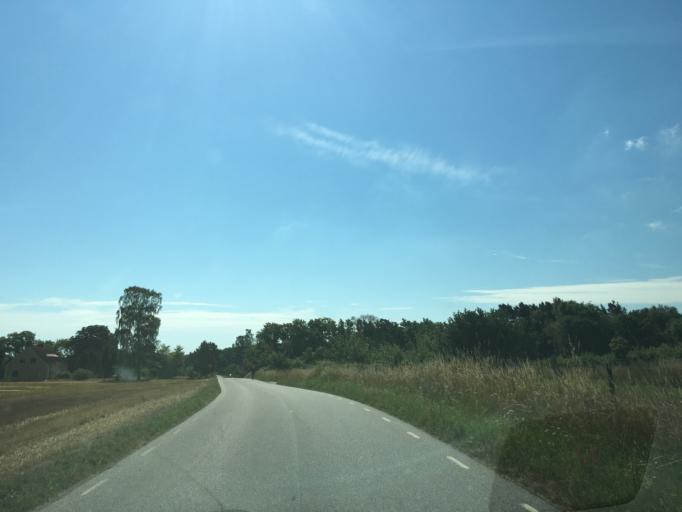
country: SE
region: Skane
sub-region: Simrishamns Kommun
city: Simrishamn
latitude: 55.5988
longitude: 14.2996
